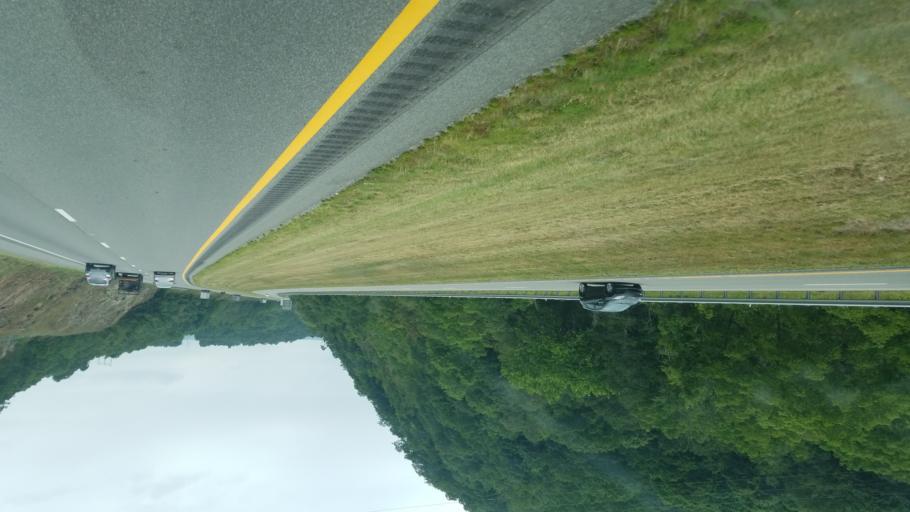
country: US
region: Virginia
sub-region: Wythe County
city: Wytheville
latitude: 36.9902
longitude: -81.0767
